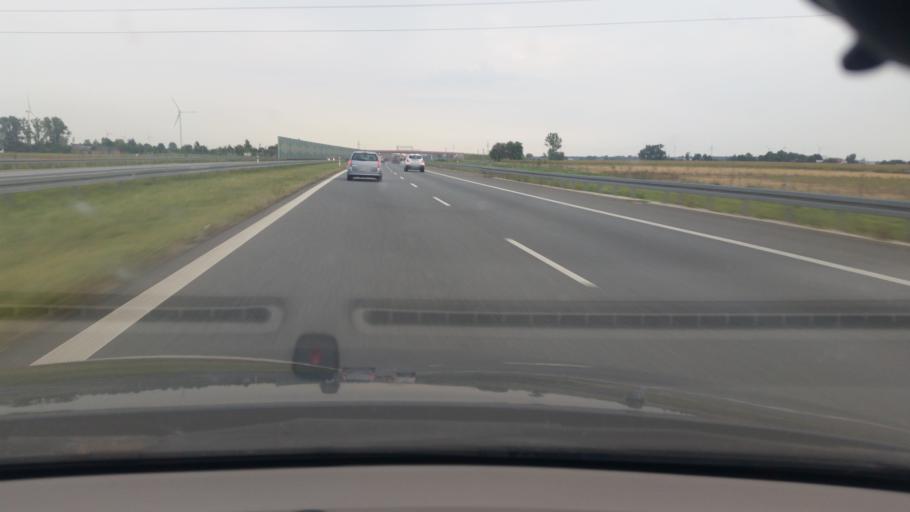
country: PL
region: Lodz Voivodeship
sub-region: Powiat kutnowski
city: Krzyzanow
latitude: 52.2494
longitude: 19.4467
